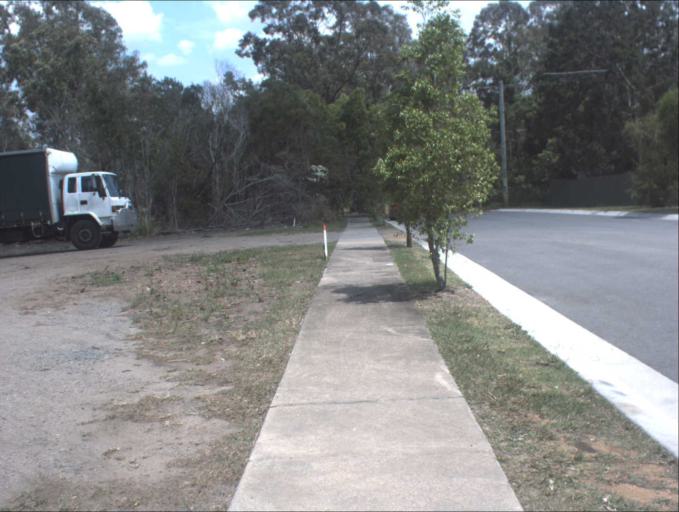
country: AU
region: Queensland
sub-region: Logan
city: Slacks Creek
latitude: -27.6477
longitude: 153.1562
